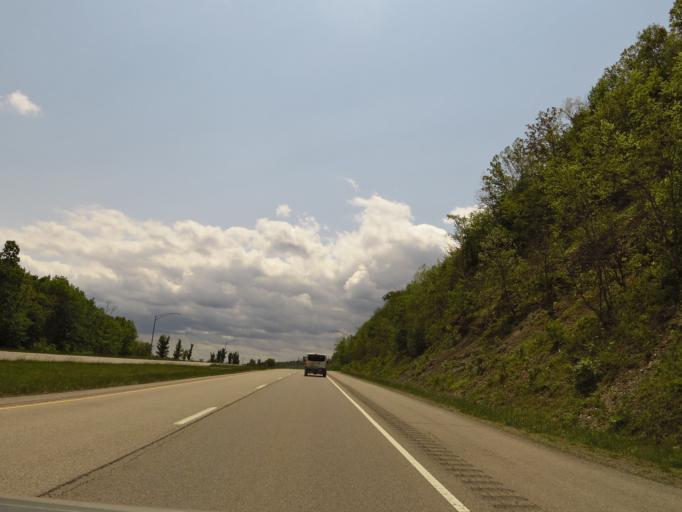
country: US
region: Ohio
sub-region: Meigs County
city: Pomeroy
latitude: 39.0631
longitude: -82.0185
